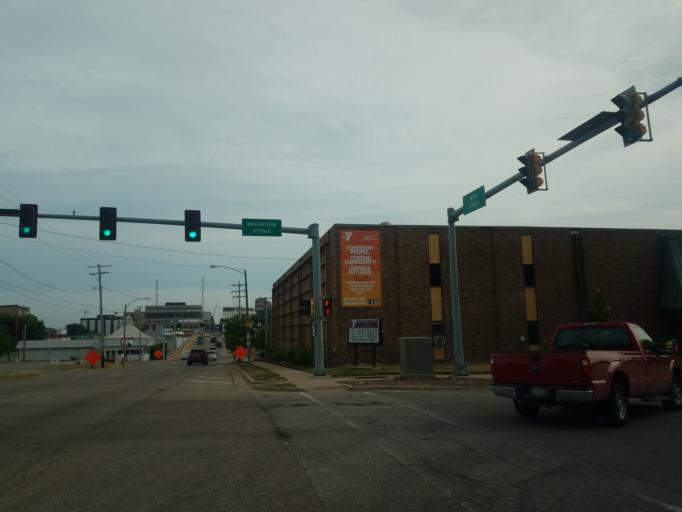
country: US
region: Illinois
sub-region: McLean County
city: Bloomington
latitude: 40.4729
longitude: -88.9933
